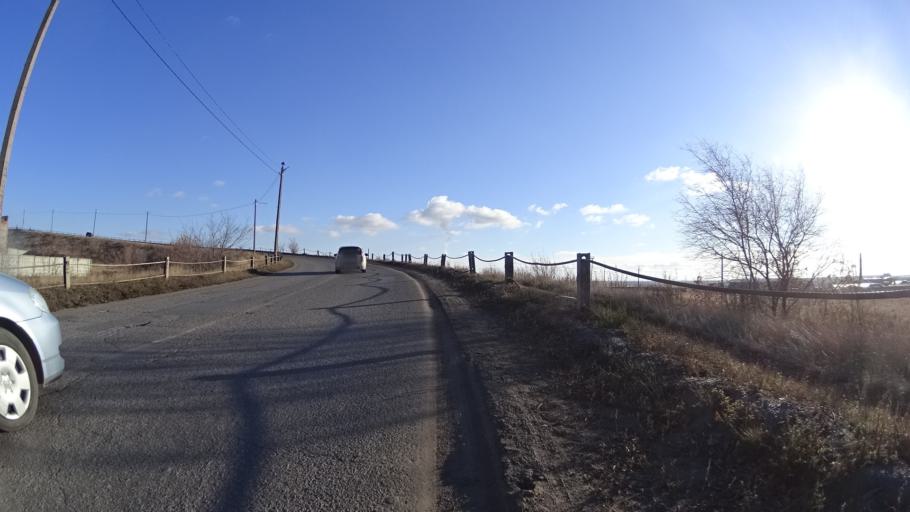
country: RU
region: Chelyabinsk
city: Troitsk
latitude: 54.0802
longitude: 61.5981
